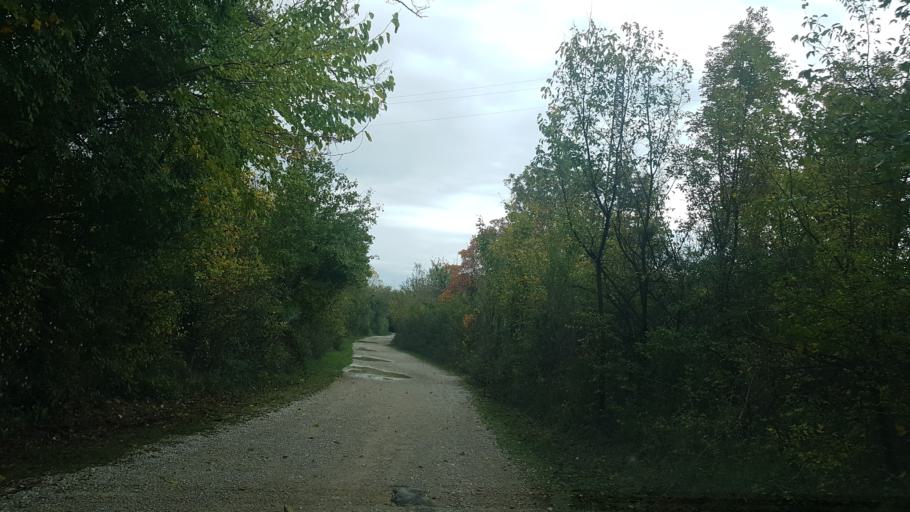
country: IT
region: Friuli Venezia Giulia
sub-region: Provincia di Gorizia
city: Ronchi dei Legionari
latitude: 45.8201
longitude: 13.5222
